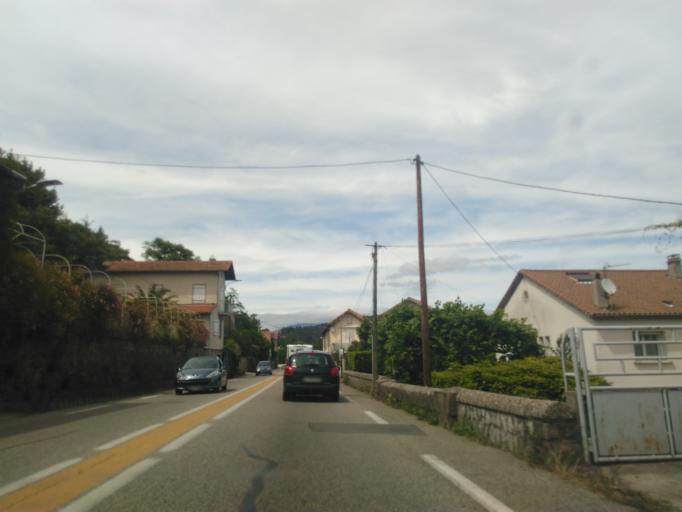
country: FR
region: Rhone-Alpes
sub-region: Departement de l'Ardeche
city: Aubenas
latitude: 44.6330
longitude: 4.3798
